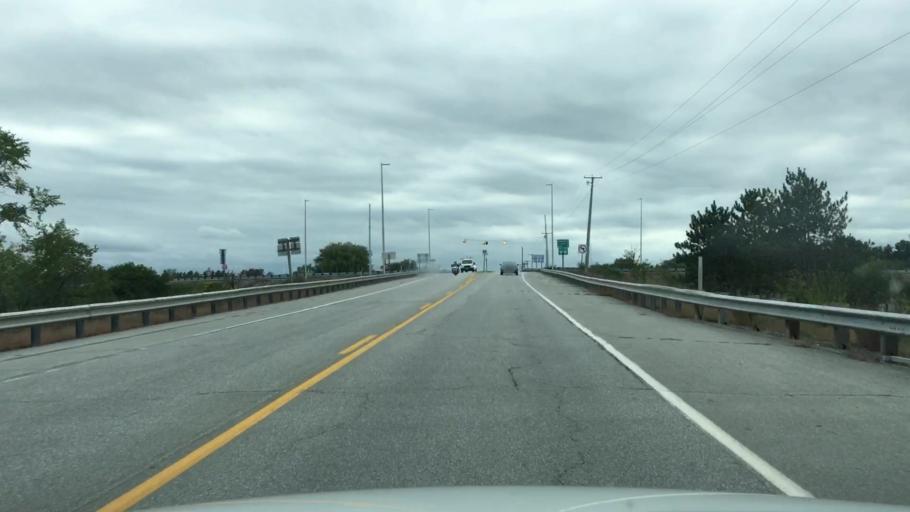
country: US
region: Maine
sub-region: Kennebec County
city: Gardiner
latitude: 44.2098
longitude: -69.8215
